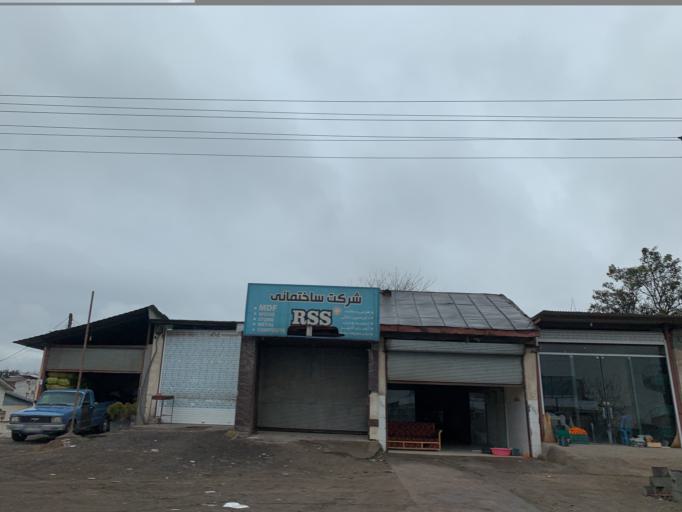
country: IR
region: Mazandaran
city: Amol
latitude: 36.4088
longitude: 52.3483
